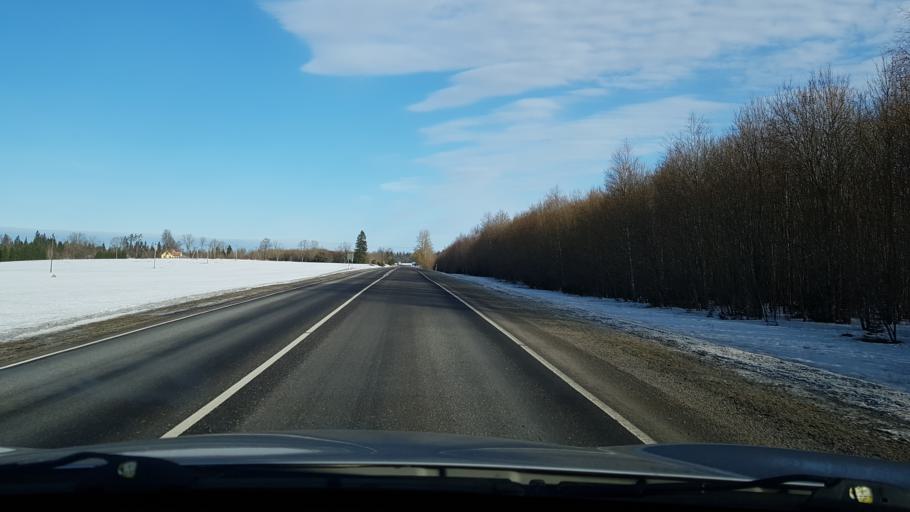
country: EE
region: Viljandimaa
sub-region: Viljandi linn
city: Viljandi
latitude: 58.4144
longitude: 25.5957
